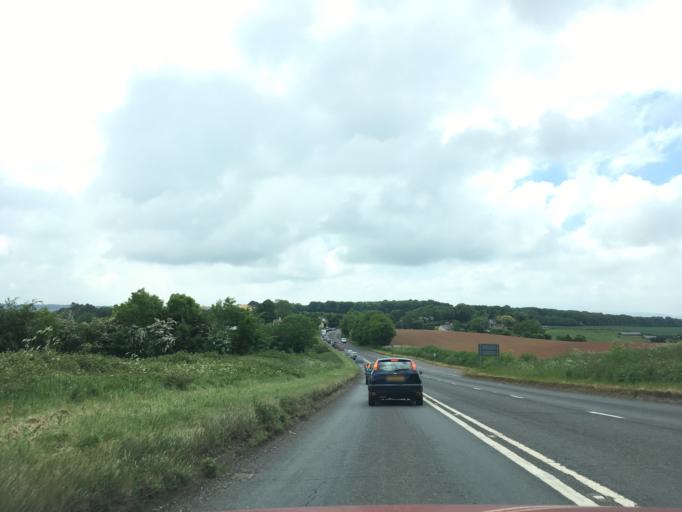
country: GB
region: England
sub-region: Devon
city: Uffculme
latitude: 50.9263
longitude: -3.3236
